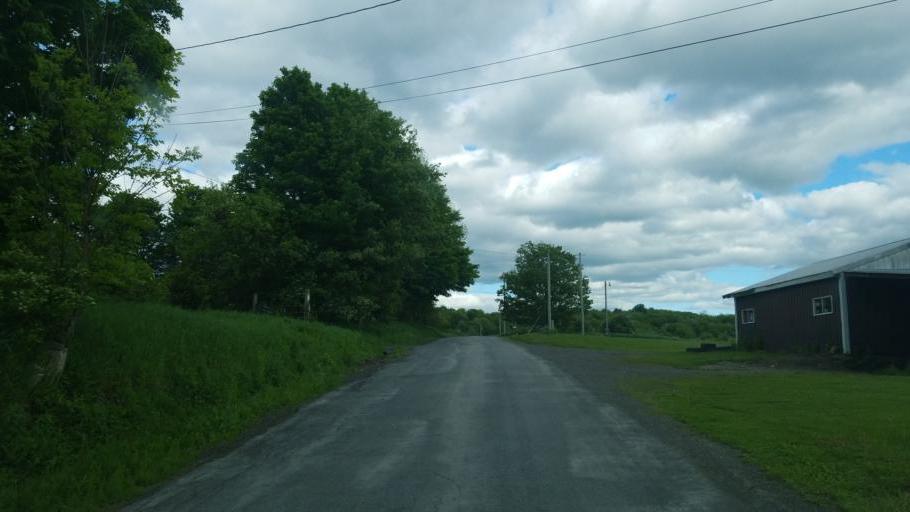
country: US
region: New York
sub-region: Otsego County
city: Richfield Springs
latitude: 42.8195
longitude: -74.9693
